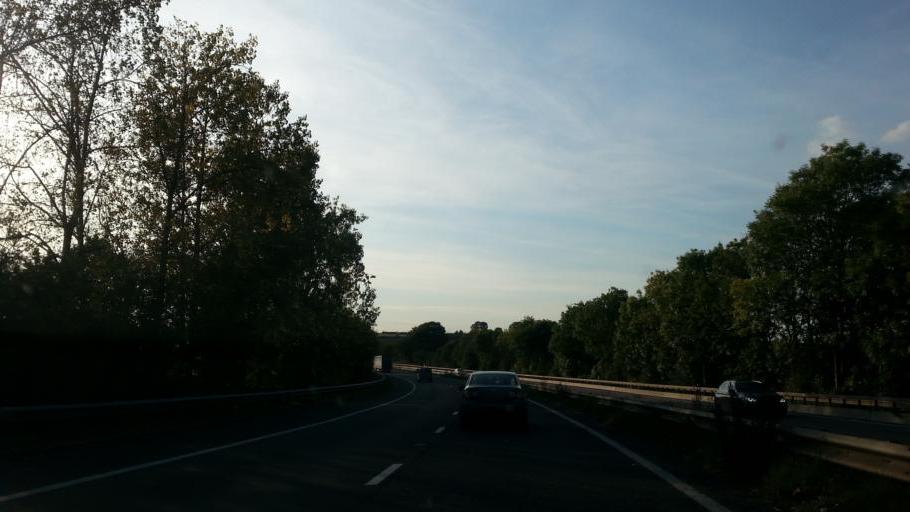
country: GB
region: England
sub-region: Herefordshire
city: Linton
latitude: 51.9312
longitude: -2.5131
